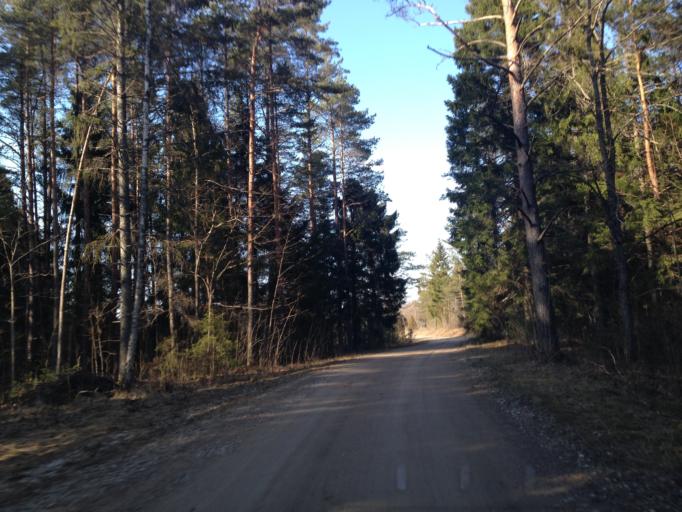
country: EE
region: Harju
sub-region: Nissi vald
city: Turba
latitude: 59.1107
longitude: 24.1570
